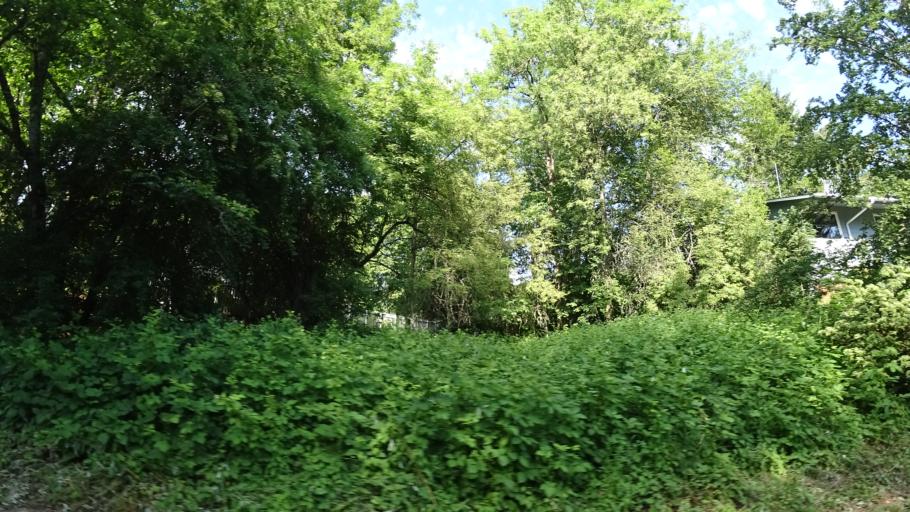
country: US
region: Oregon
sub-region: Washington County
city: Garden Home-Whitford
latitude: 45.4598
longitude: -122.7339
